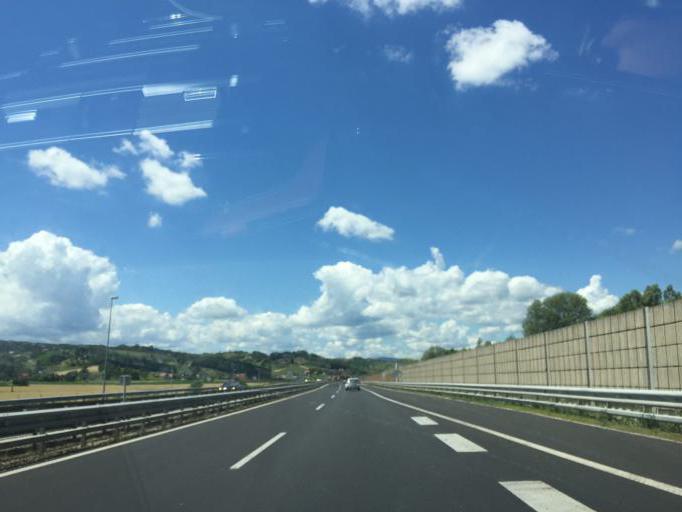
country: SI
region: Sveti Jurij v Slovenskih Goricah
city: Jurovski Dol
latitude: 46.5751
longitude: 15.7485
